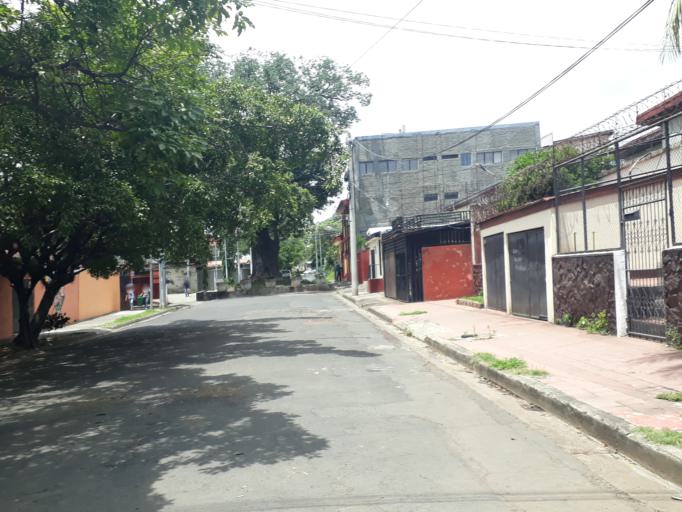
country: NI
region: Managua
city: Managua
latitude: 12.1442
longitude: -86.2767
